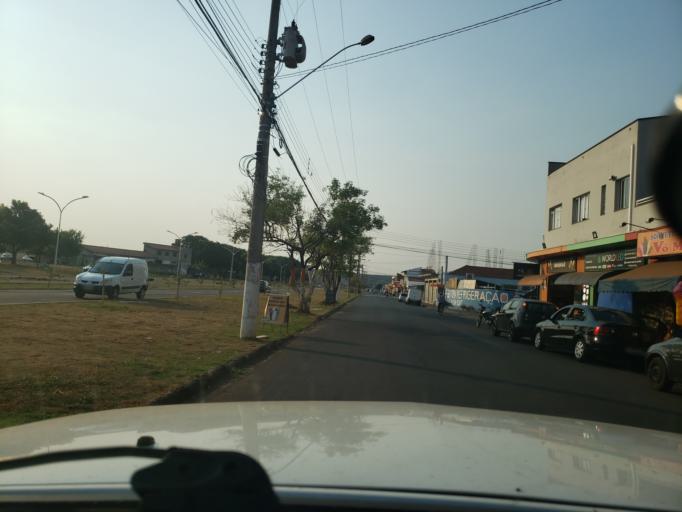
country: BR
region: Sao Paulo
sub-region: Moji-Guacu
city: Mogi-Gaucu
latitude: -22.3354
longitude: -46.9452
